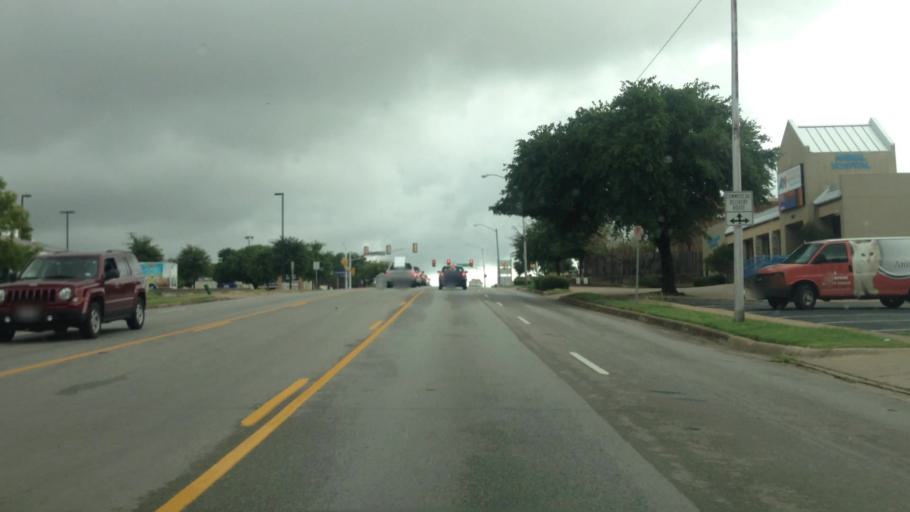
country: US
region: Texas
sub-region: Tarrant County
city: Edgecliff Village
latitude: 32.6495
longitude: -97.3960
